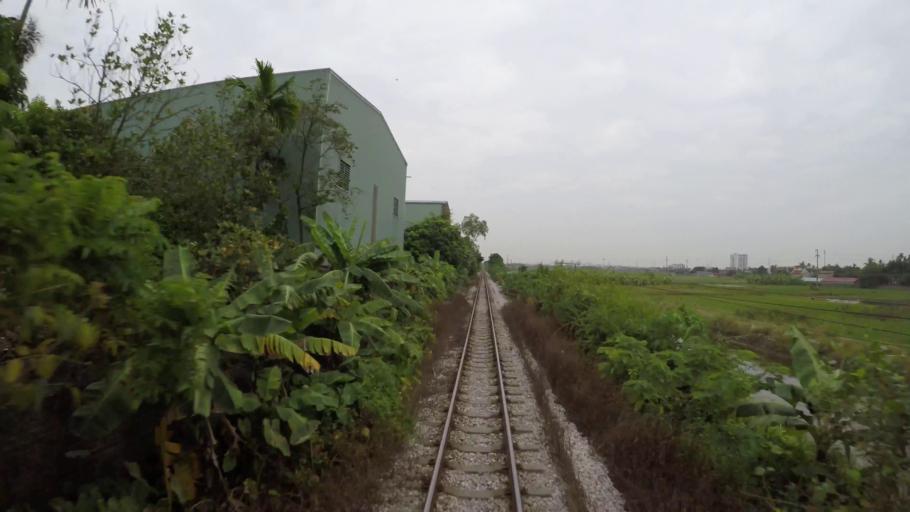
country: VN
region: Hai Phong
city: An Duong
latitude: 20.8967
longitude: 106.5840
